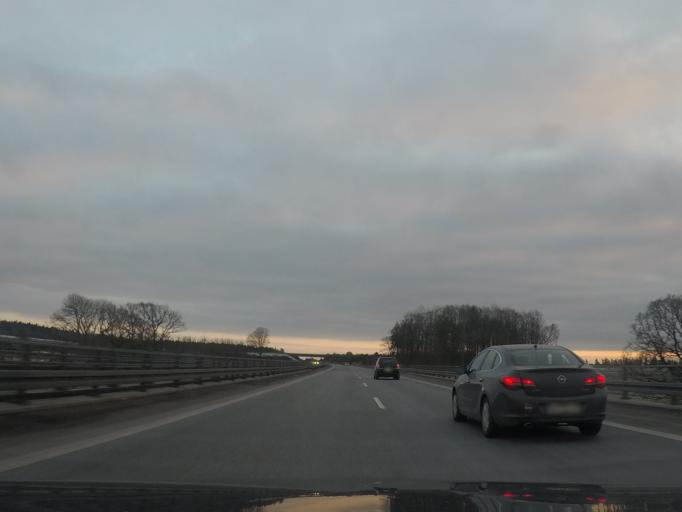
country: DK
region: Central Jutland
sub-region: Herning Kommune
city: Lind
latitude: 56.0776
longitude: 8.9971
